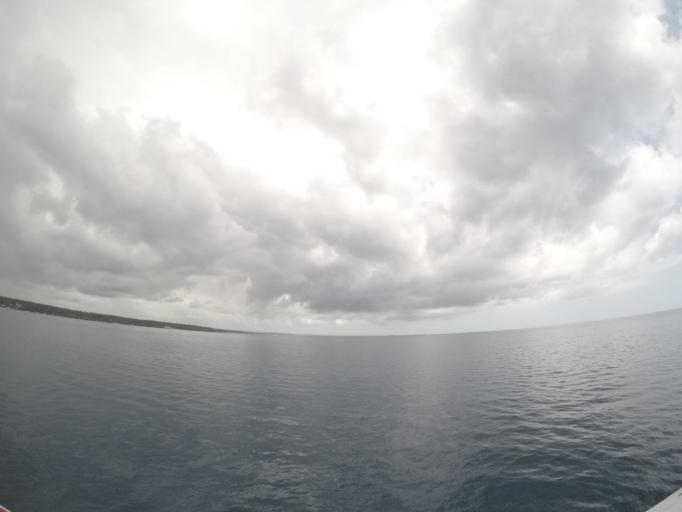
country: TZ
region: Zanzibar North
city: Mkokotoni
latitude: -5.9778
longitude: 39.1721
